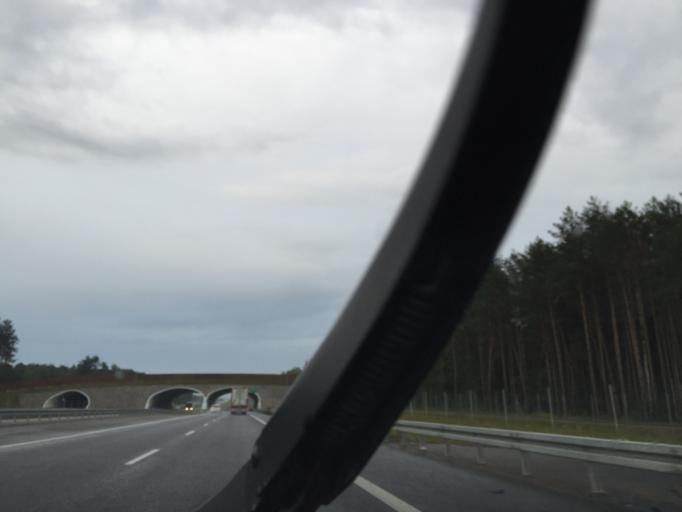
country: PL
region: Podlasie
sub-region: Powiat zambrowski
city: Zambrow
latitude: 53.0250
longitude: 22.3265
